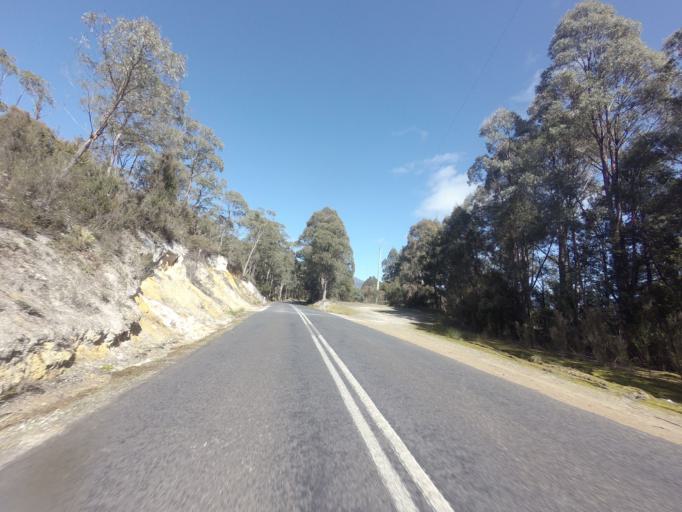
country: AU
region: Tasmania
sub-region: Derwent Valley
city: New Norfolk
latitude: -42.7687
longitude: 146.5786
